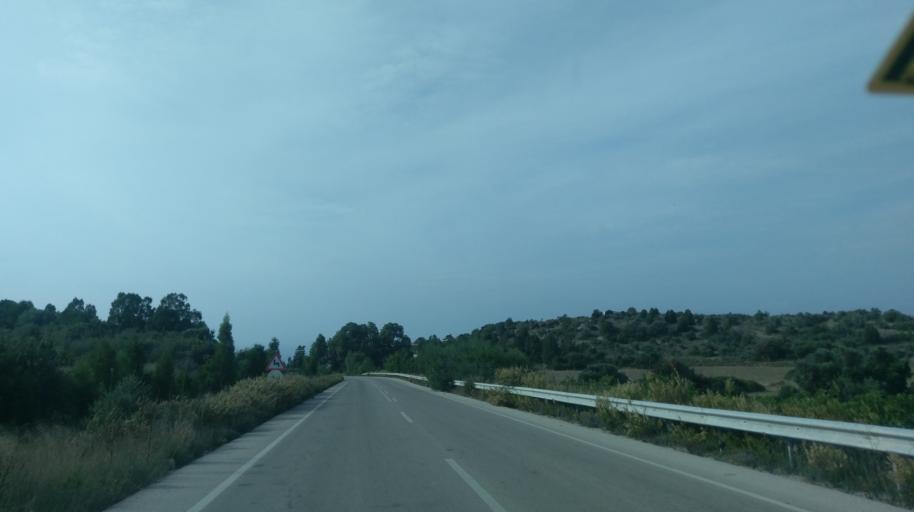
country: CY
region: Ammochostos
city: Trikomo
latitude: 35.4290
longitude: 33.9757
